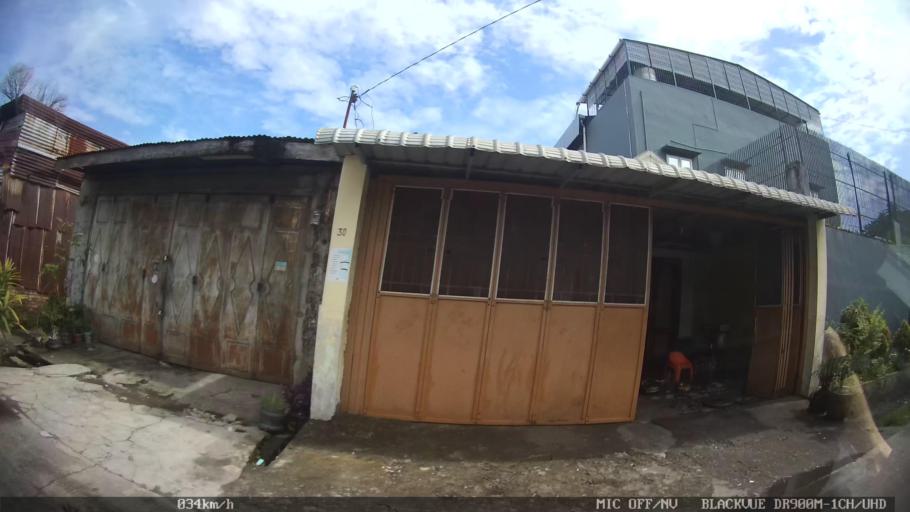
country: ID
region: North Sumatra
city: Medan
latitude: 3.5874
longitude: 98.7140
